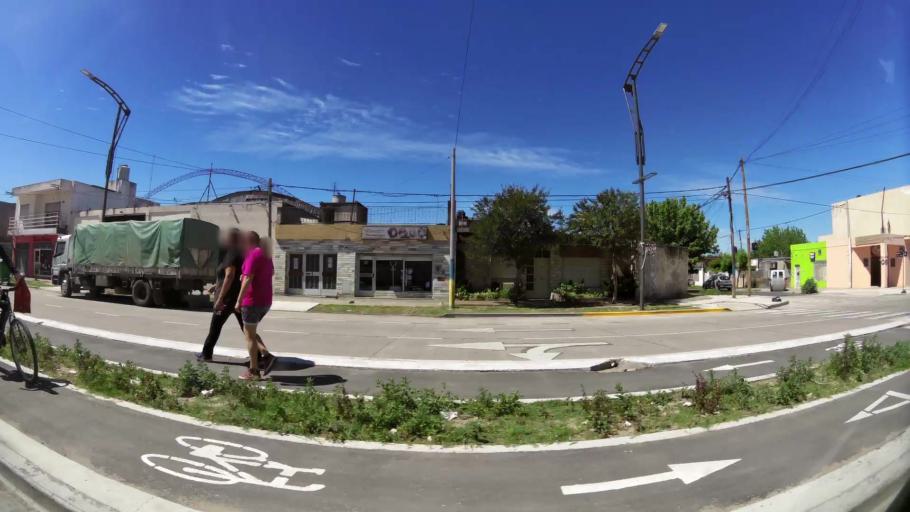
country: AR
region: Santa Fe
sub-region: Departamento de Rosario
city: Rosario
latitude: -32.9589
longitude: -60.7037
